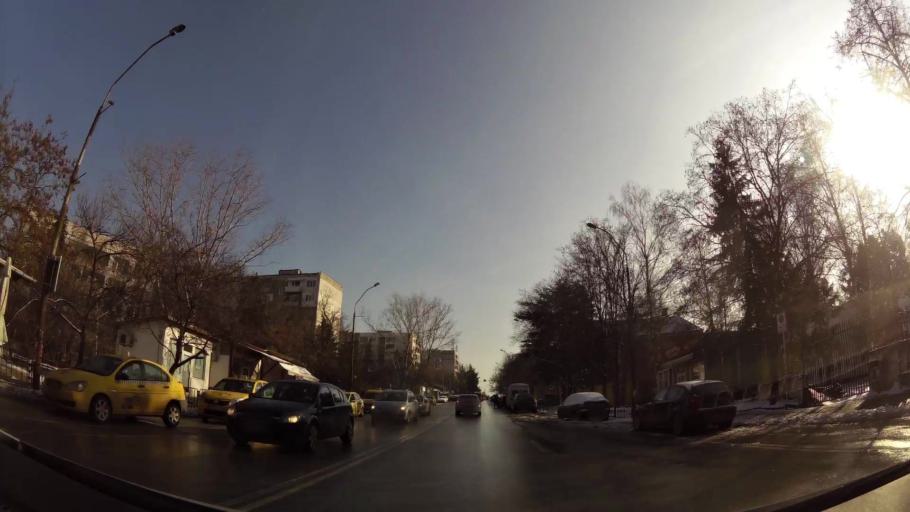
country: BG
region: Sofia-Capital
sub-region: Stolichna Obshtina
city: Sofia
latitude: 42.6624
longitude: 23.3454
